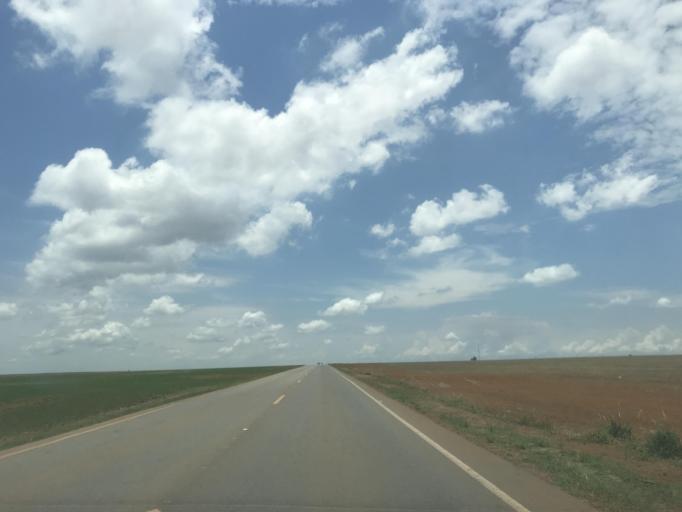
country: BR
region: Goias
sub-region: Vianopolis
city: Vianopolis
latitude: -16.5170
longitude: -48.2358
